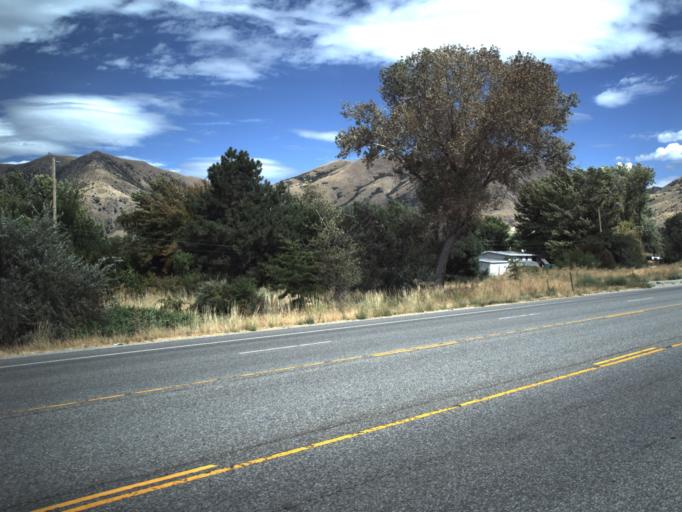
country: US
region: Utah
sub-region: Box Elder County
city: Perry
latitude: 41.4865
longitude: -112.0233
